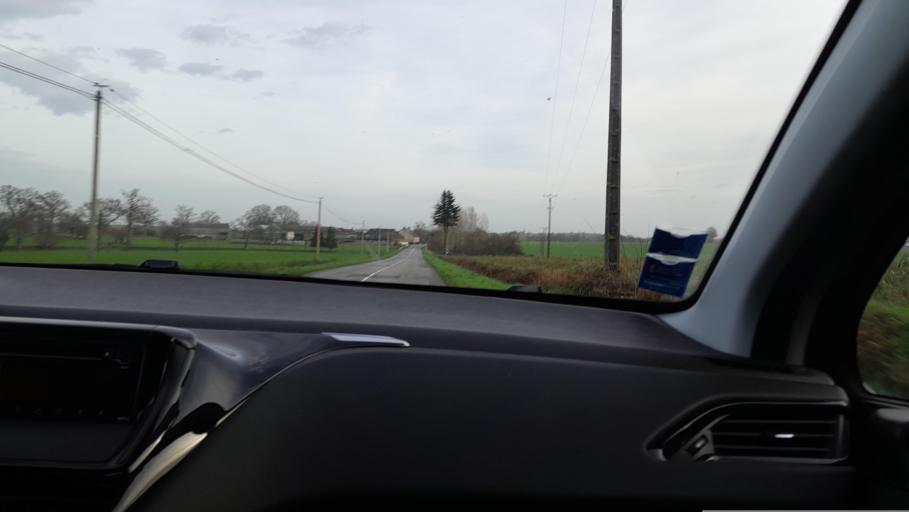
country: FR
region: Brittany
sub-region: Departement d'Ille-et-Vilaine
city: La Guerche-de-Bretagne
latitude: 47.9616
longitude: -1.1487
